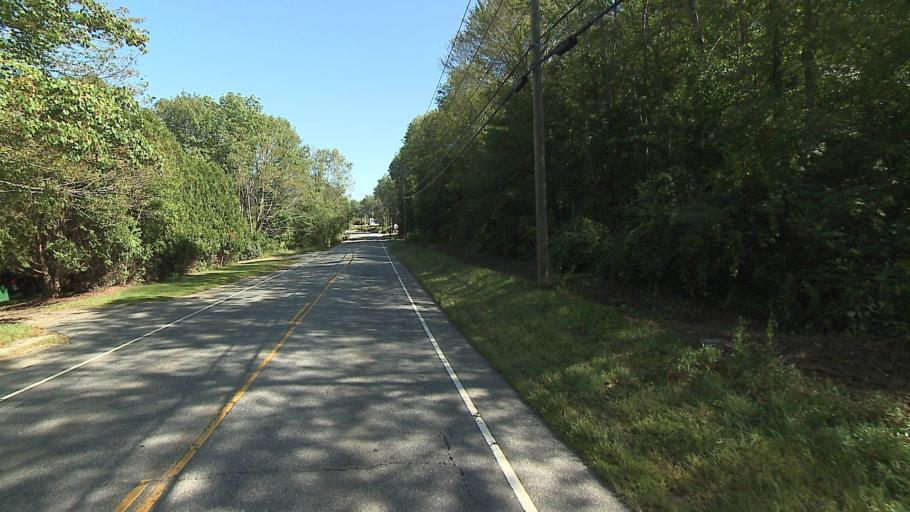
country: US
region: Connecticut
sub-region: Windham County
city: Plainfield
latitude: 41.7006
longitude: -71.9073
